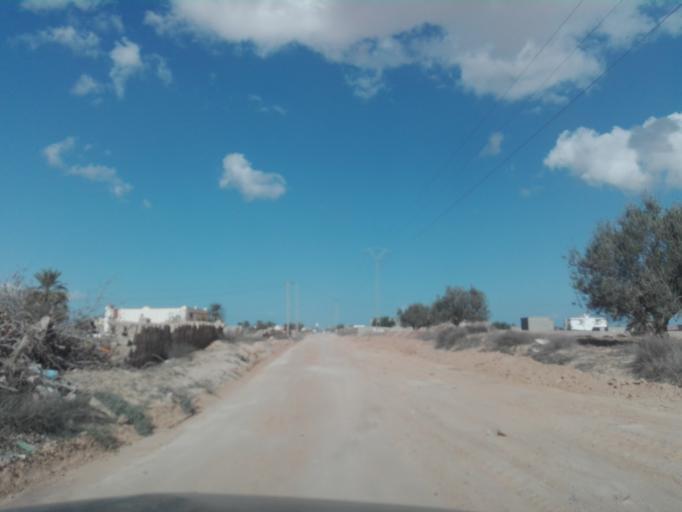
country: TN
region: Madanin
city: Bin Qirdan
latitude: 33.1493
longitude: 11.1923
